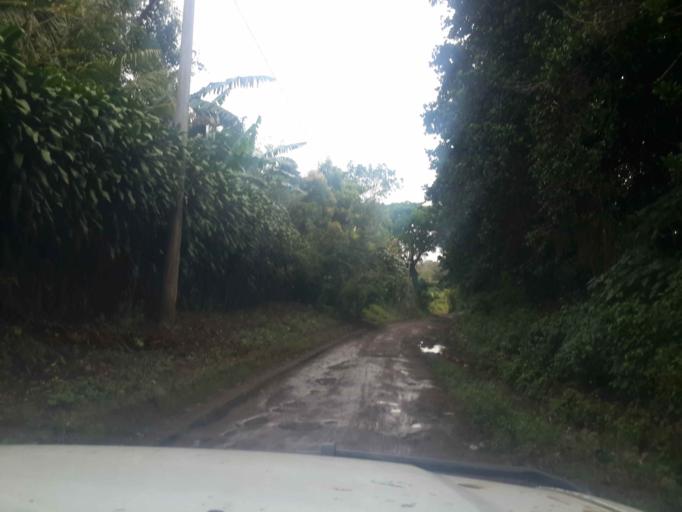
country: NI
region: Carazo
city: San Marcos
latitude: 11.8850
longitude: -86.1867
